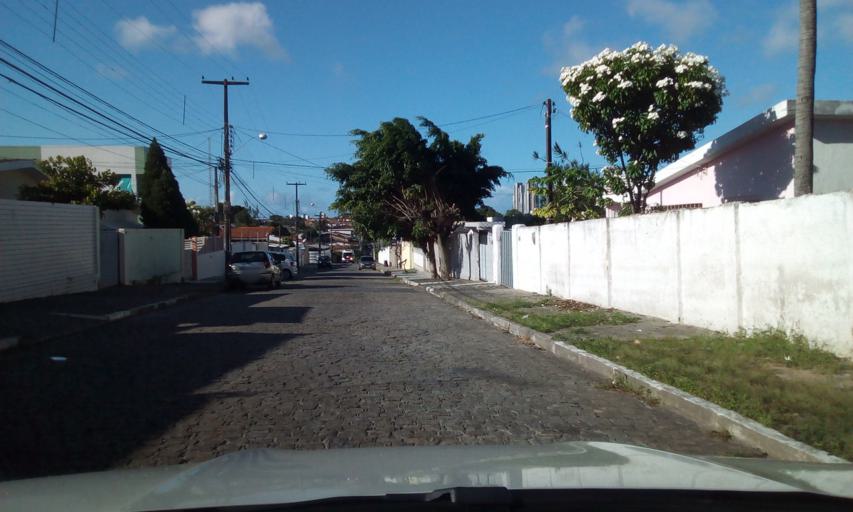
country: BR
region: Paraiba
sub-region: Joao Pessoa
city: Joao Pessoa
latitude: -7.1110
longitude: -34.8614
